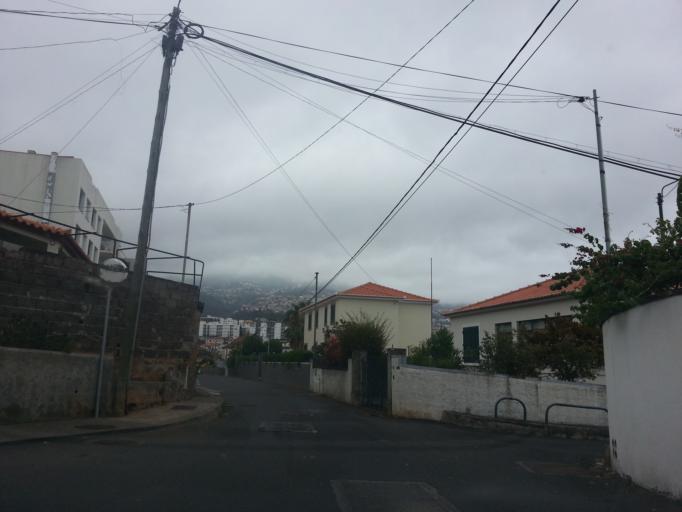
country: PT
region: Madeira
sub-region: Funchal
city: Funchal
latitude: 32.6491
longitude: -16.9287
